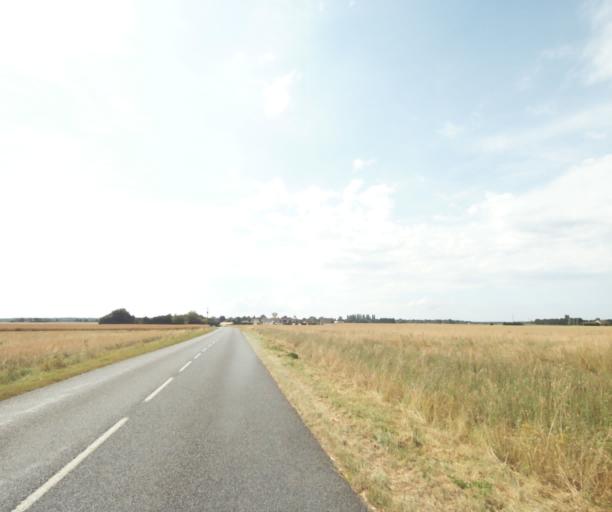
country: FR
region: Ile-de-France
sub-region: Departement de Seine-et-Marne
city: Acheres-la-Foret
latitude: 48.3490
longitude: 2.5826
